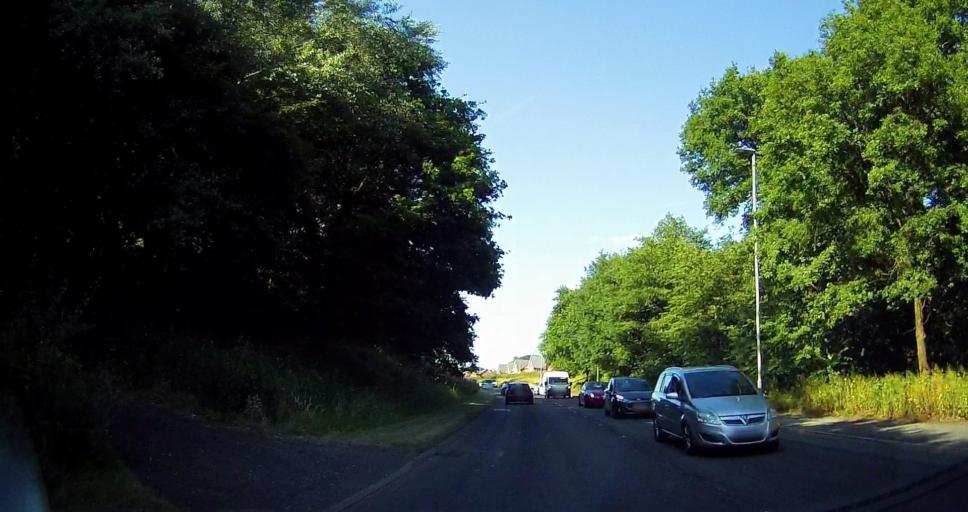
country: GB
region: England
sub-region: Cheshire East
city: Sandbach
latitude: 53.1469
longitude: -2.3530
